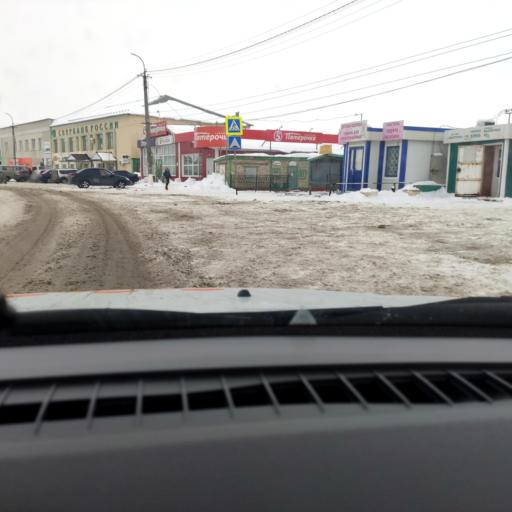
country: RU
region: Saratov
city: Perelyub
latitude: 52.0958
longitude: 50.8665
